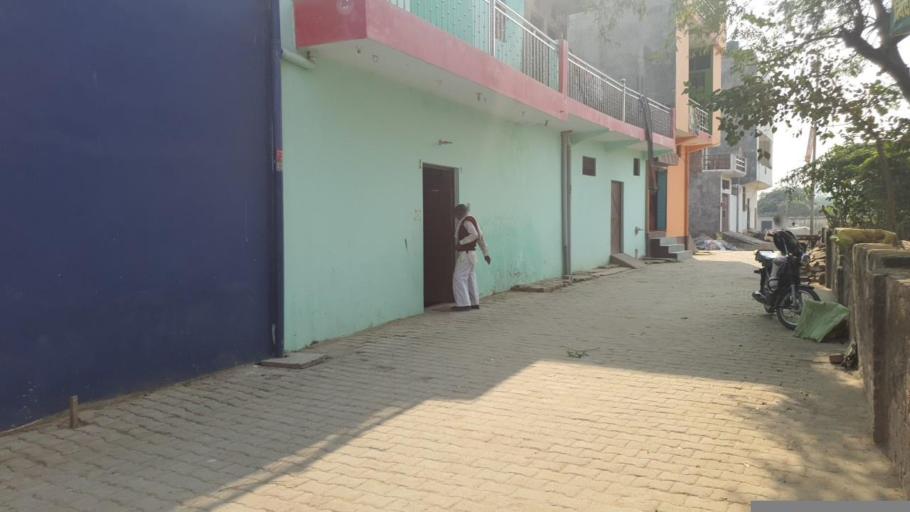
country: IN
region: Uttar Pradesh
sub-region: Lucknow District
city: Lucknow
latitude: 26.8003
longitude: 81.0050
